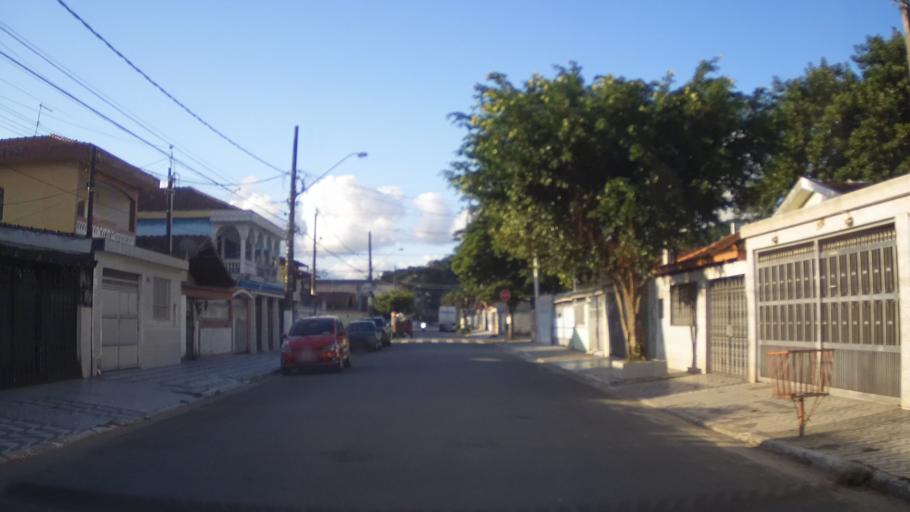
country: BR
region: Sao Paulo
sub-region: Praia Grande
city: Praia Grande
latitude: -24.0070
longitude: -46.4115
